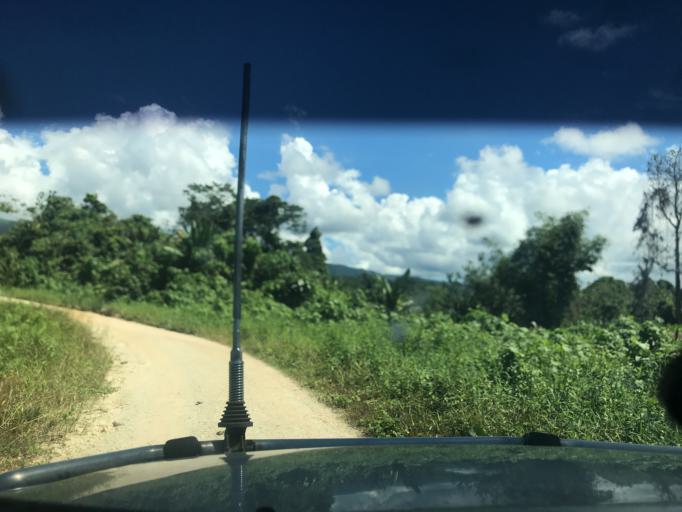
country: SB
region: Malaita
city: Auki
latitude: -8.7273
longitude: 160.9041
